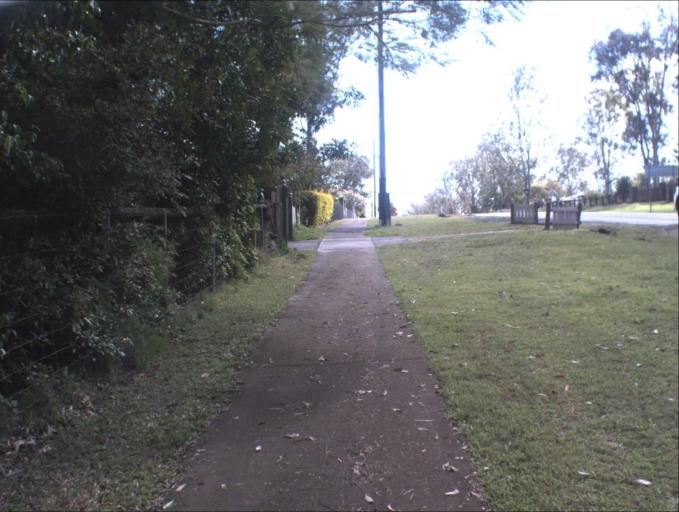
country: AU
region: Queensland
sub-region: Logan
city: Park Ridge South
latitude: -27.7158
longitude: 152.9767
